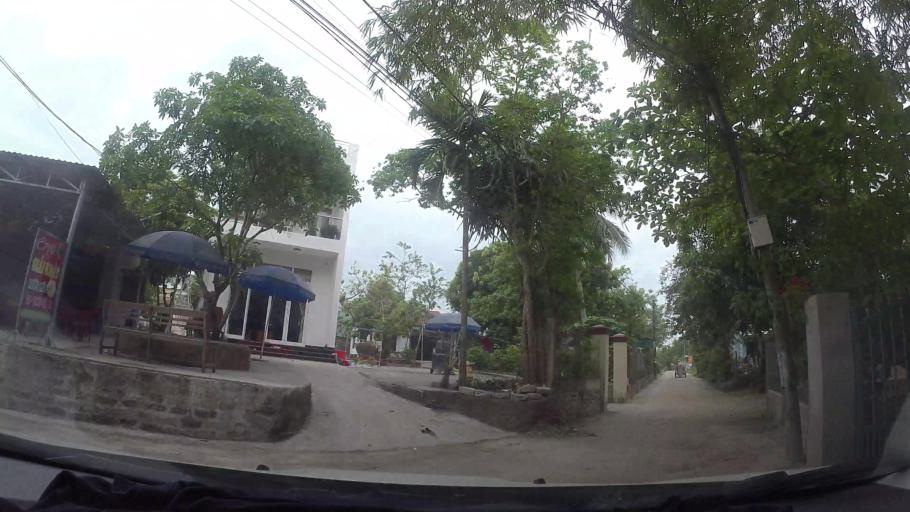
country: VN
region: Da Nang
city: Lien Chieu
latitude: 16.0766
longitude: 108.0967
